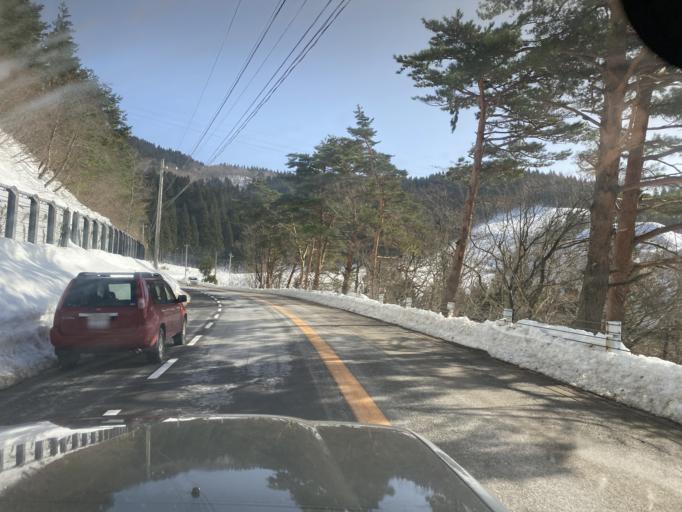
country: JP
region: Toyama
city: Fukumitsu
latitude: 36.4696
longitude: 136.8967
